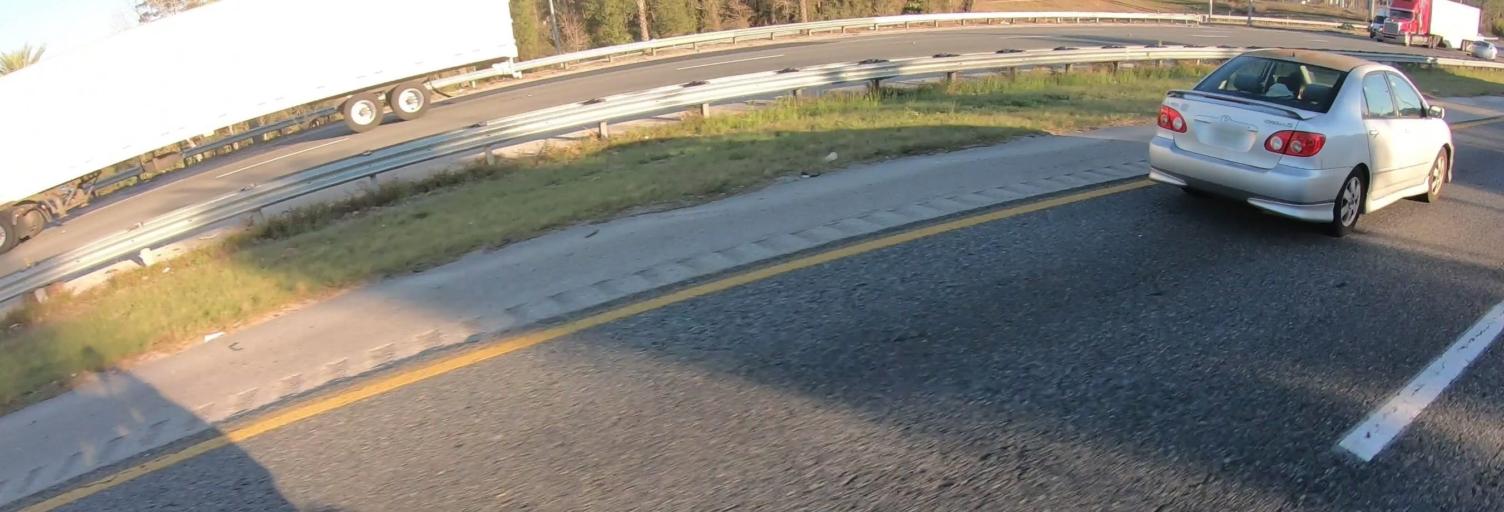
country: US
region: Florida
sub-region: Marion County
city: Ocala
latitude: 29.1469
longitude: -82.1864
